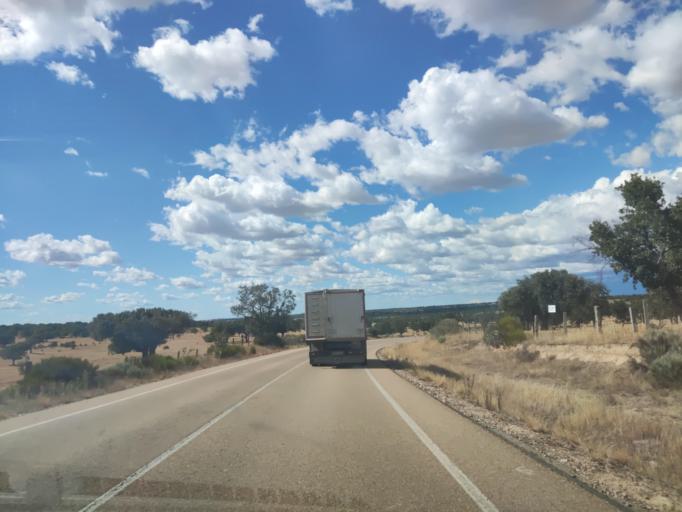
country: ES
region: Castille and Leon
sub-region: Provincia de Salamanca
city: Peralejos de Arriba
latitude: 40.9324
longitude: -6.3415
